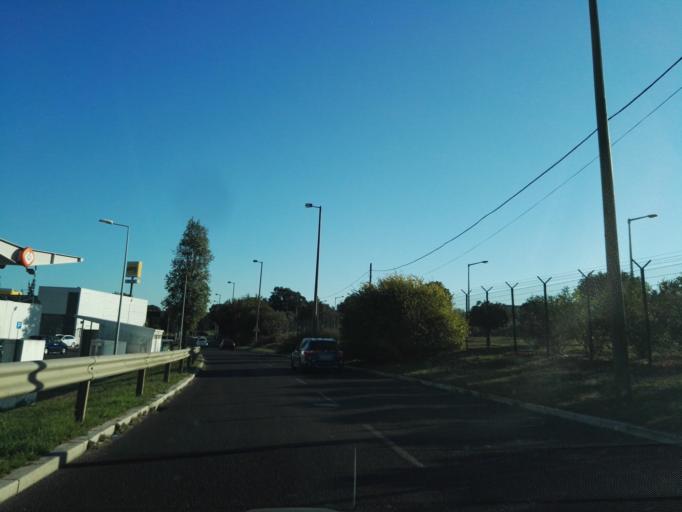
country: PT
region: Lisbon
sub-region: Loures
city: Sacavem
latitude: 38.7800
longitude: -9.1244
